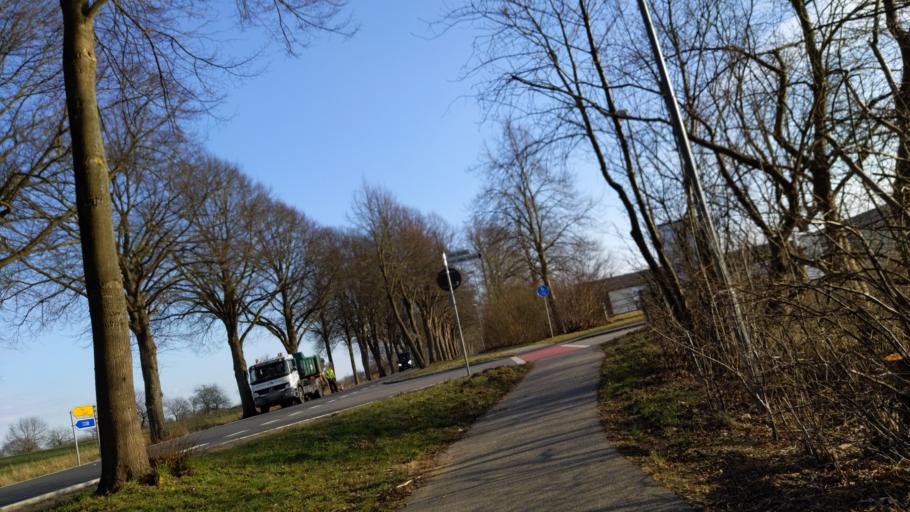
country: DE
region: Schleswig-Holstein
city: Ratekau
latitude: 53.9577
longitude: 10.7244
